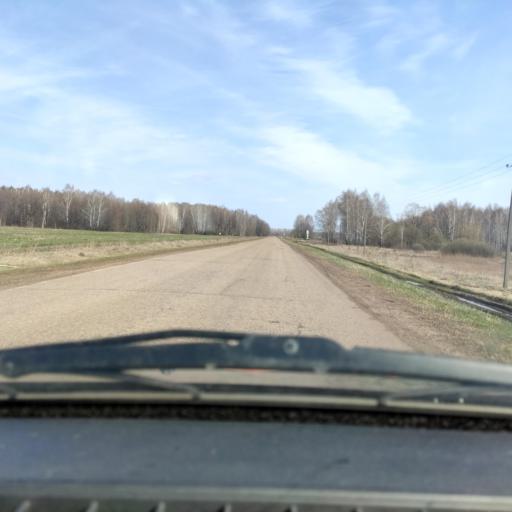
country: RU
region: Bashkortostan
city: Asanovo
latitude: 54.7974
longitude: 55.5296
